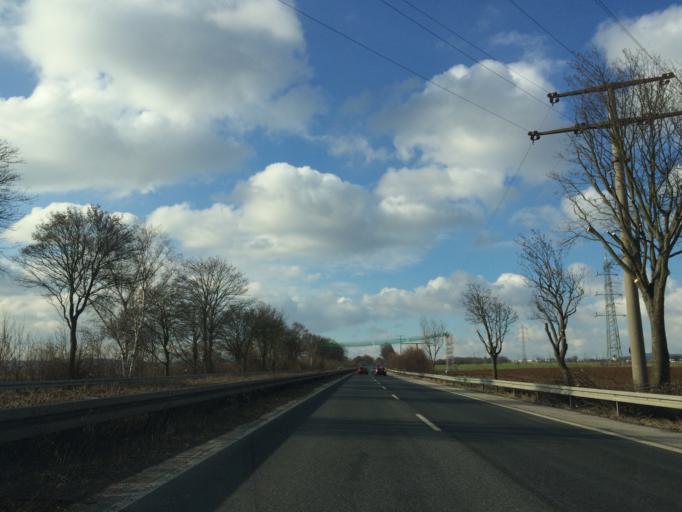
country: DE
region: Hesse
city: Liederbach
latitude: 50.1244
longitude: 8.5114
